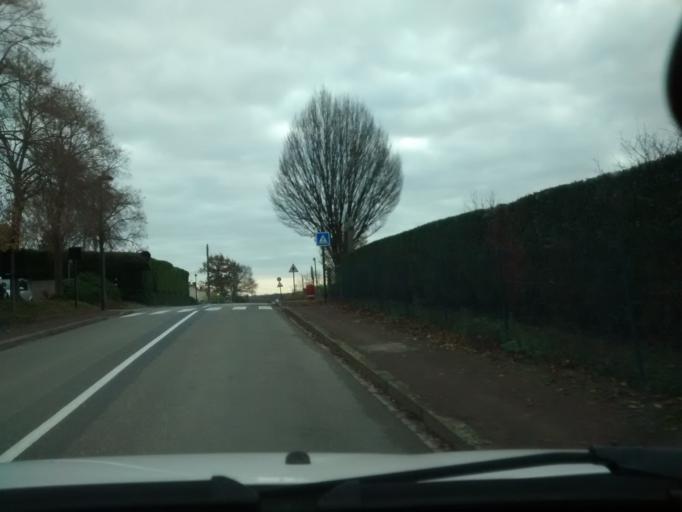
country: FR
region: Brittany
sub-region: Departement d'Ille-et-Vilaine
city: Chavagne
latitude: 48.0793
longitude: -1.7734
